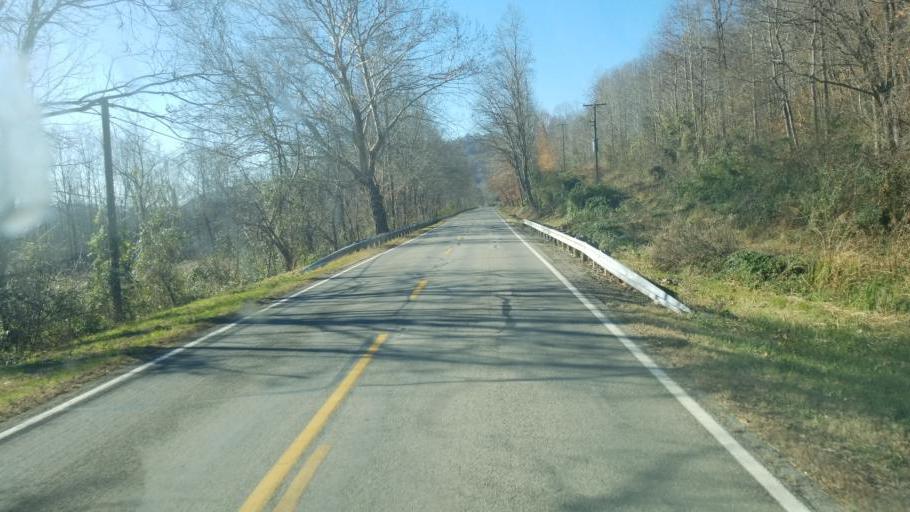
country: US
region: Kentucky
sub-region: Lewis County
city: Vanceburg
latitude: 38.6358
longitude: -83.2440
